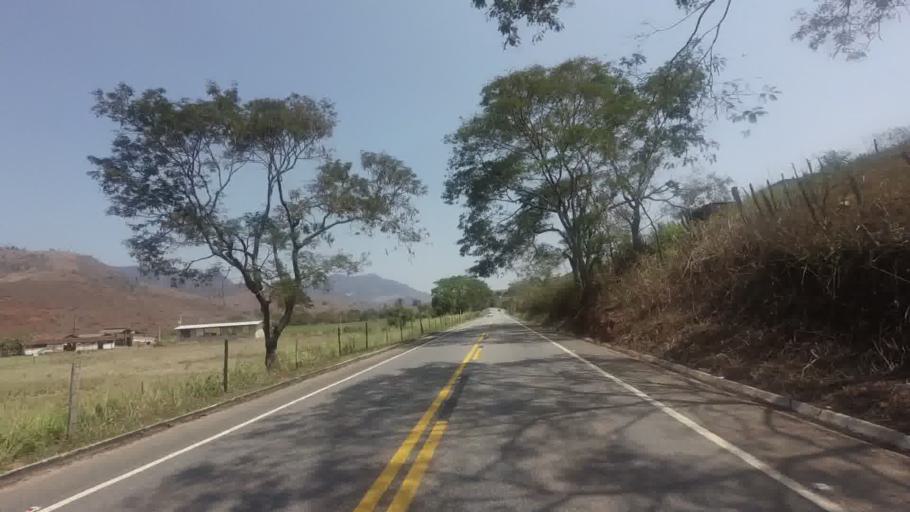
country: BR
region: Espirito Santo
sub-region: Jeronimo Monteiro
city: Jeronimo Monteiro
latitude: -20.9172
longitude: -41.3054
